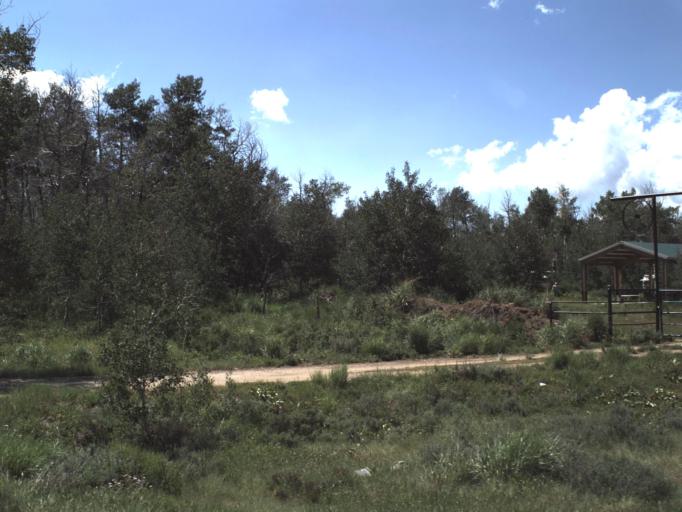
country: US
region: Utah
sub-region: Weber County
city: Wolf Creek
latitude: 41.4210
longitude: -111.5628
